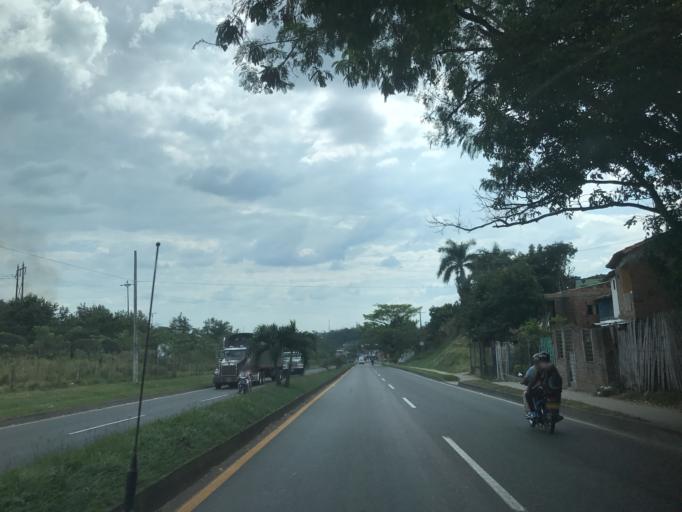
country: CO
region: Valle del Cauca
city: Cartago
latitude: 4.7625
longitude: -75.8976
